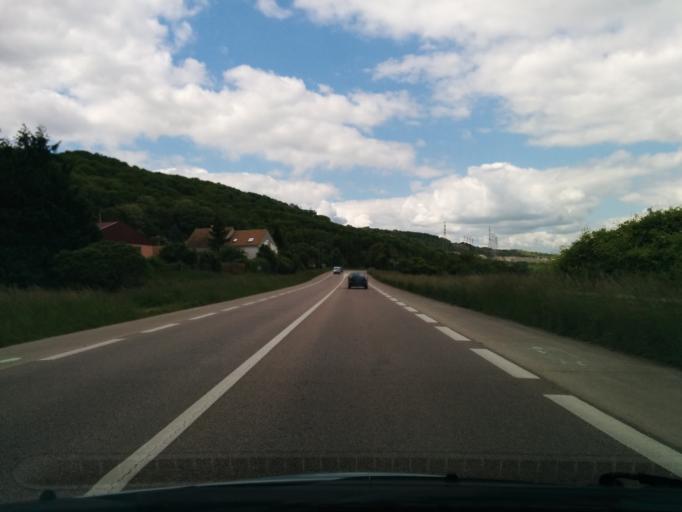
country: FR
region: Ile-de-France
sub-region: Departement des Yvelines
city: Mezieres-sur-Seine
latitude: 48.9619
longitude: 1.7883
